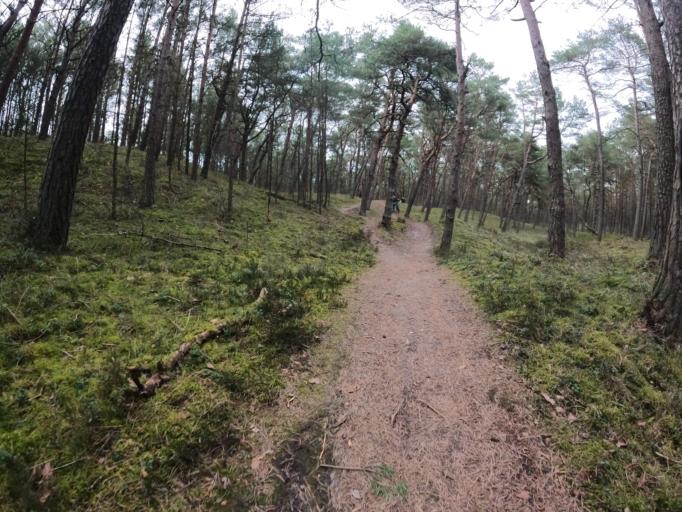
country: PL
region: West Pomeranian Voivodeship
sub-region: Powiat gryficki
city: Mrzezyno
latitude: 54.1379
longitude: 15.2641
